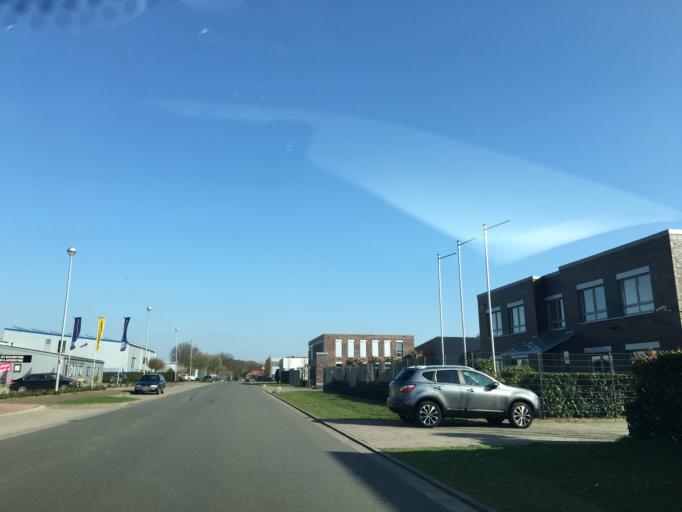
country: DE
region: North Rhine-Westphalia
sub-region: Regierungsbezirk Munster
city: Greven
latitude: 52.1106
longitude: 7.6226
